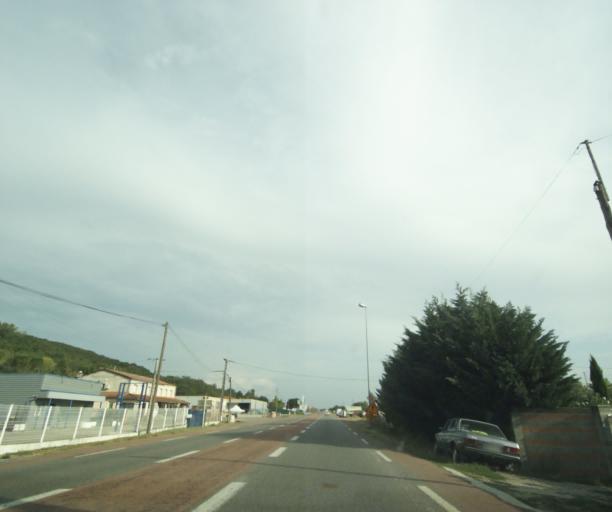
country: FR
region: Midi-Pyrenees
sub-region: Departement du Tarn-et-Garonne
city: Pompignan
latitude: 43.8125
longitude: 1.3164
